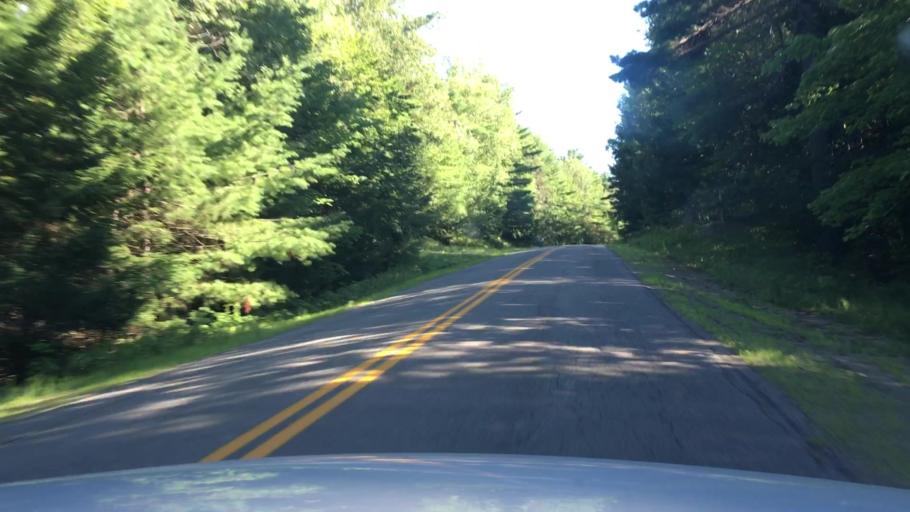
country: US
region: Maine
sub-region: Penobscot County
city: Enfield
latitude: 45.2241
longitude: -68.5801
